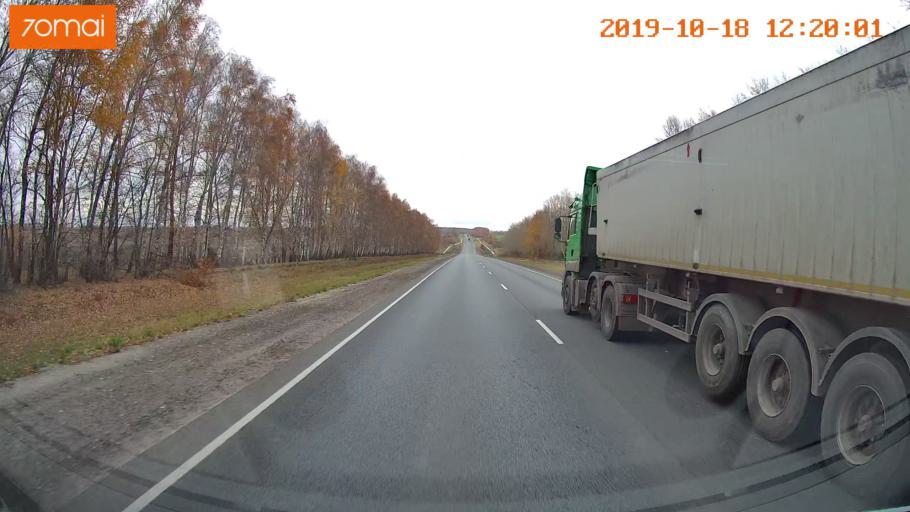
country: RU
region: Rjazan
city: Zakharovo
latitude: 54.4913
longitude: 39.4751
